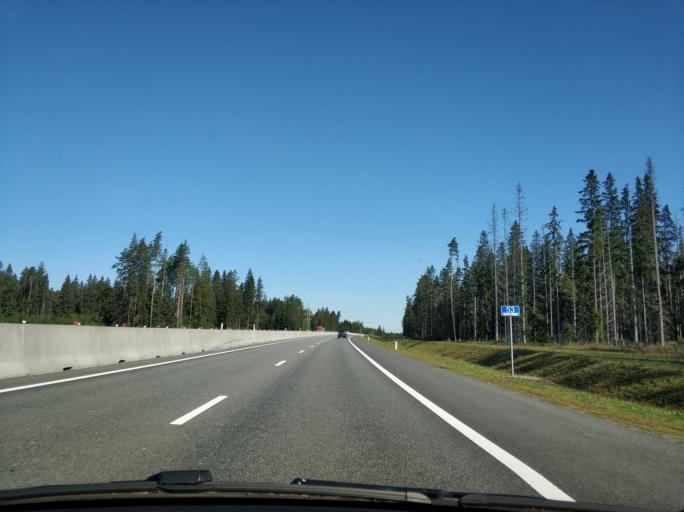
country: RU
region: Leningrad
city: Sosnovo
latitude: 60.5211
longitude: 30.1725
